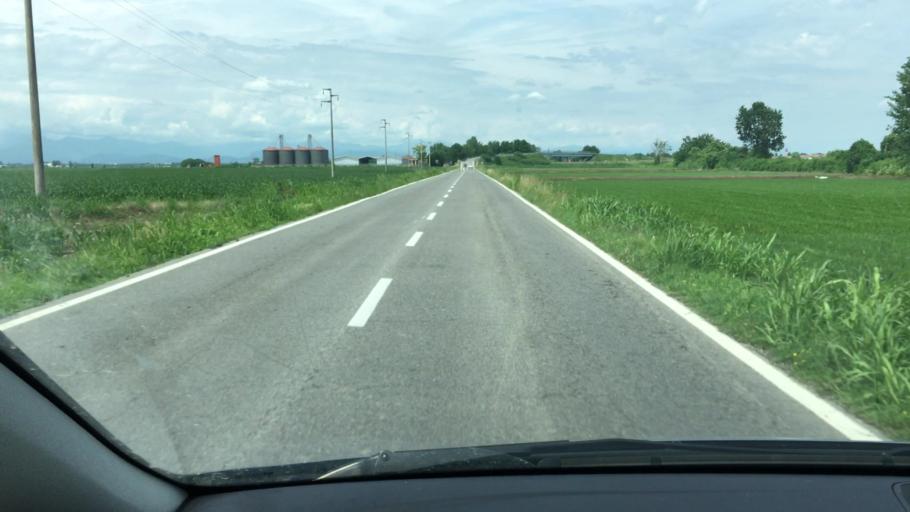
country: IT
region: Piedmont
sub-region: Provincia di Novara
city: Casalbeltrame
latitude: 45.4224
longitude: 8.4636
